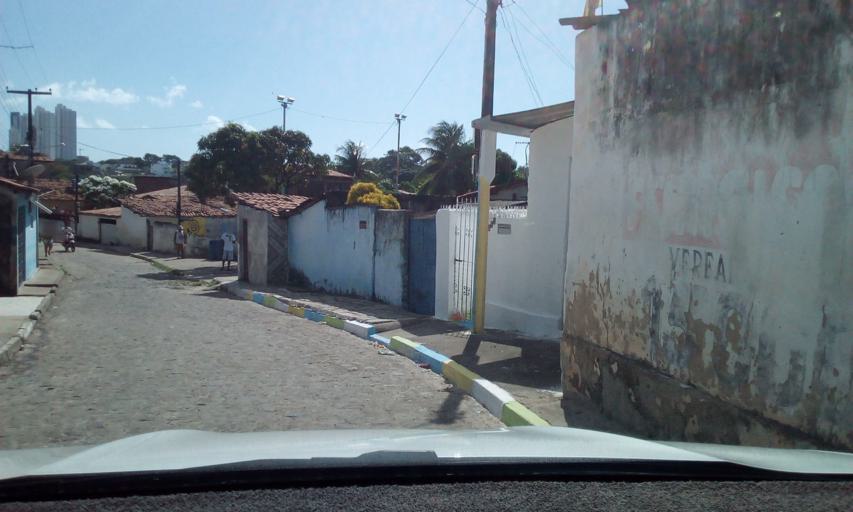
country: BR
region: Paraiba
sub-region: Joao Pessoa
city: Joao Pessoa
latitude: -7.1479
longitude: -34.8289
